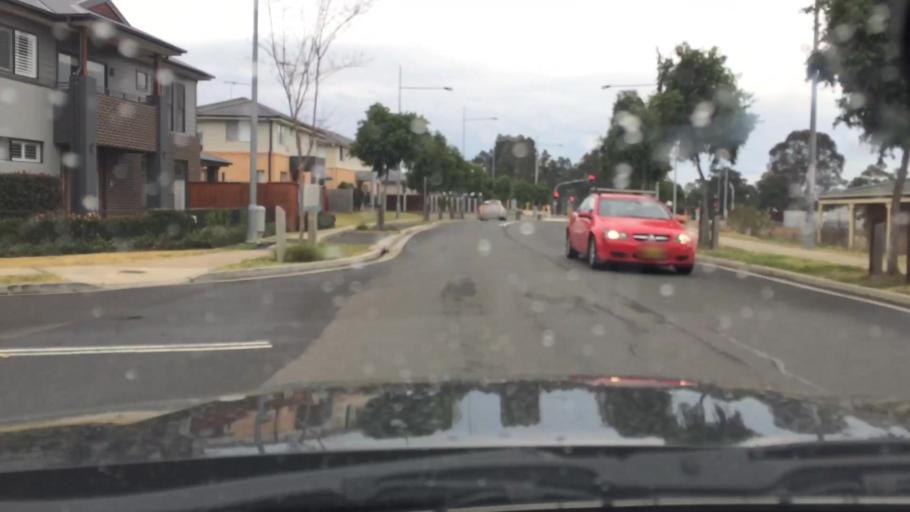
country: AU
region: New South Wales
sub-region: Campbelltown Municipality
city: Denham Court
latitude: -33.9522
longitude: 150.8452
